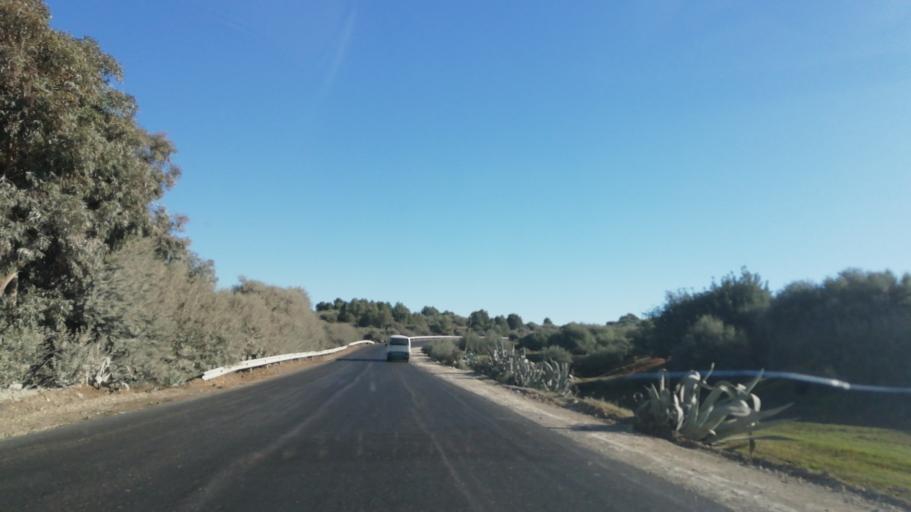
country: DZ
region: Relizane
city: Smala
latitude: 35.6675
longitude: 0.8092
